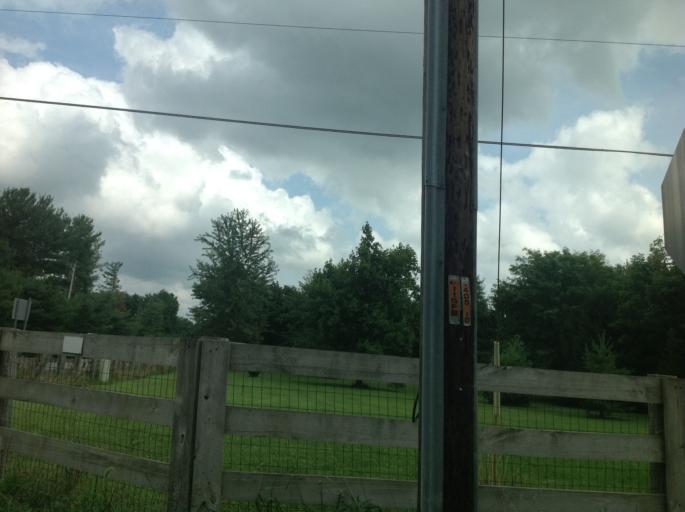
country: US
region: Ohio
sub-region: Delaware County
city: Sunbury
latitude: 40.2085
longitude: -82.9138
